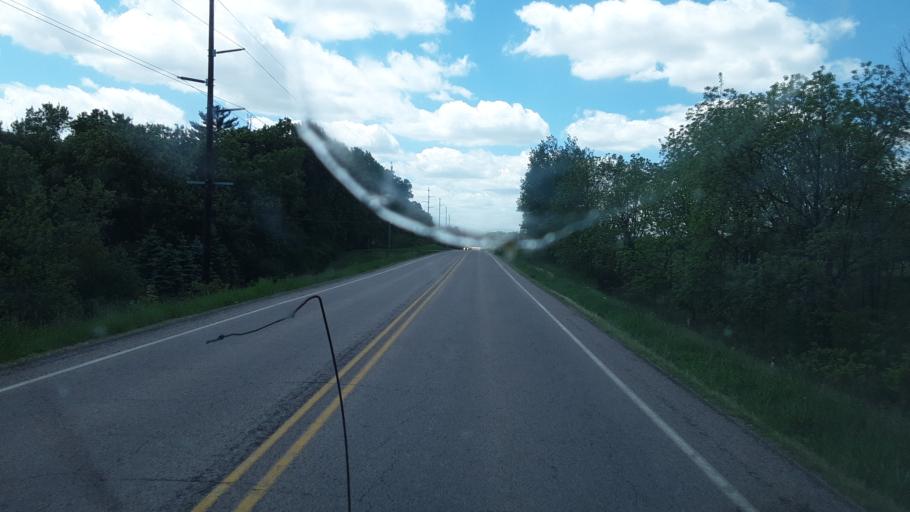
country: US
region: Wisconsin
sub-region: Sauk County
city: Lake Delton
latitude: 43.5909
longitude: -89.8635
